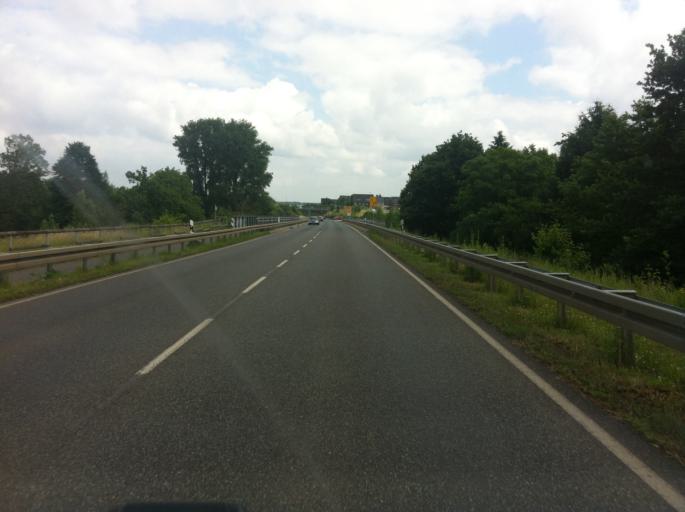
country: DE
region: North Rhine-Westphalia
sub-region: Regierungsbezirk Koln
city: Weilerswist
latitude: 50.7484
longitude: 6.8306
